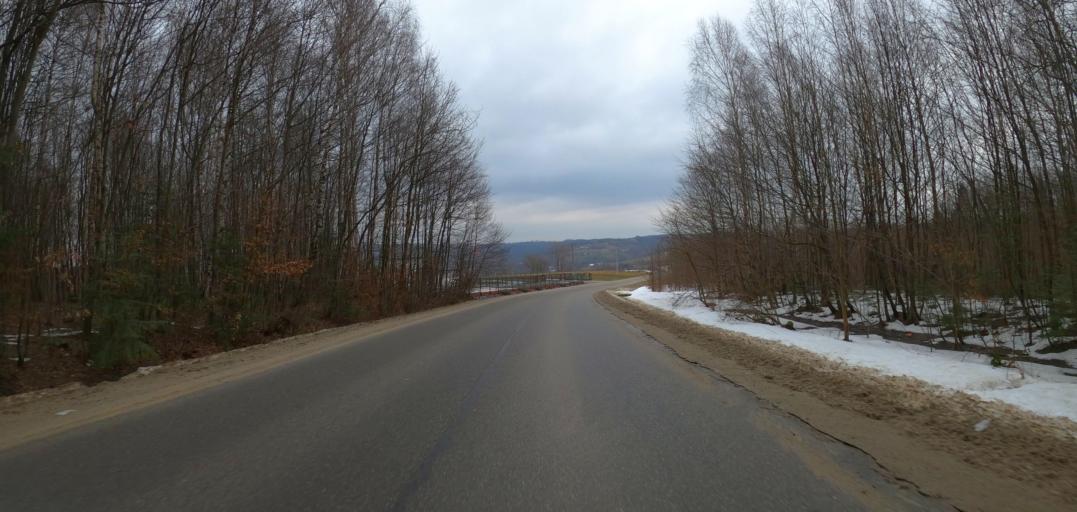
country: PL
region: Subcarpathian Voivodeship
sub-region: Powiat debicki
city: Debica
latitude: 49.9863
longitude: 21.4155
